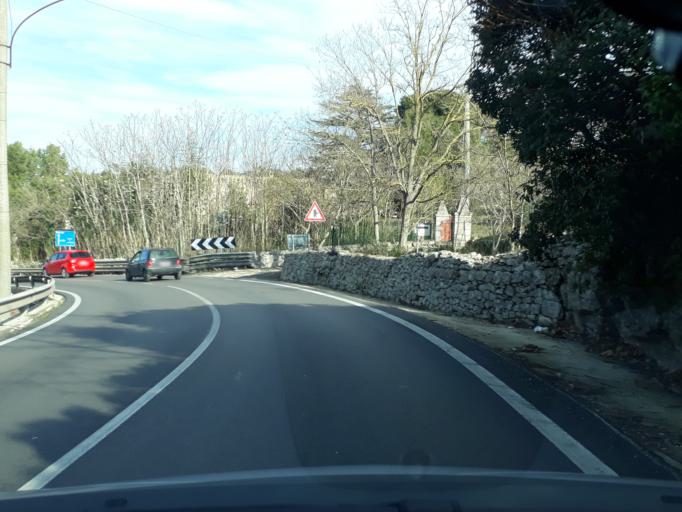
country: IT
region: Apulia
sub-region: Provincia di Brindisi
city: Lamie di Olimpie-Selva
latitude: 40.7976
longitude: 17.3515
